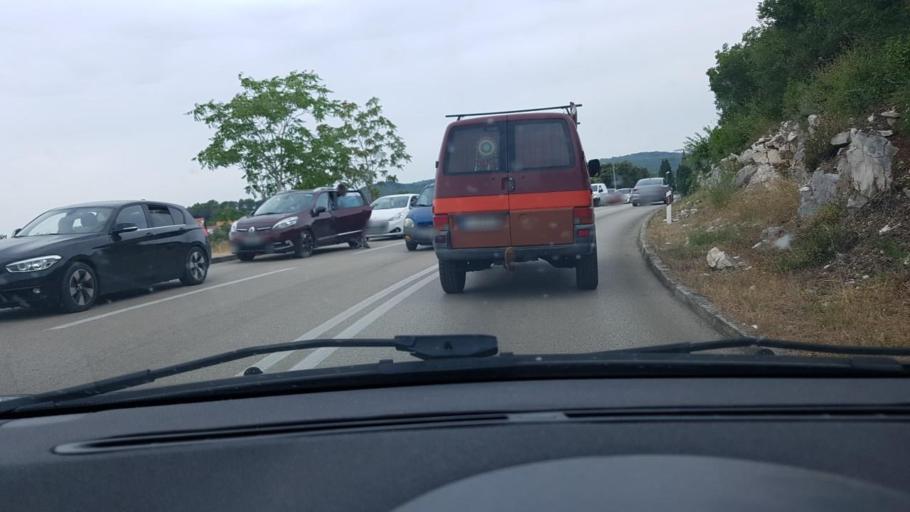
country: HR
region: Dubrovacko-Neretvanska
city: Korcula
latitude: 42.9527
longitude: 17.1485
